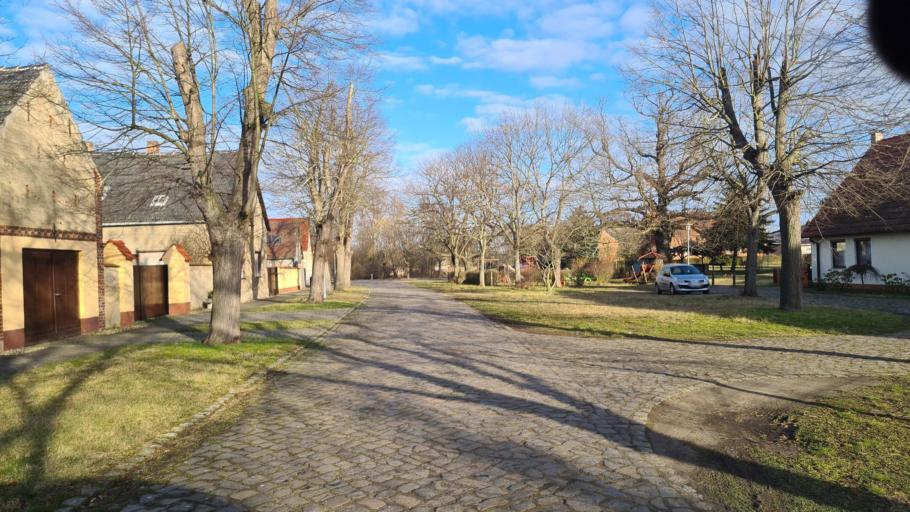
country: DE
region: Brandenburg
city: Herzberg
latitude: 51.7145
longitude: 13.2060
